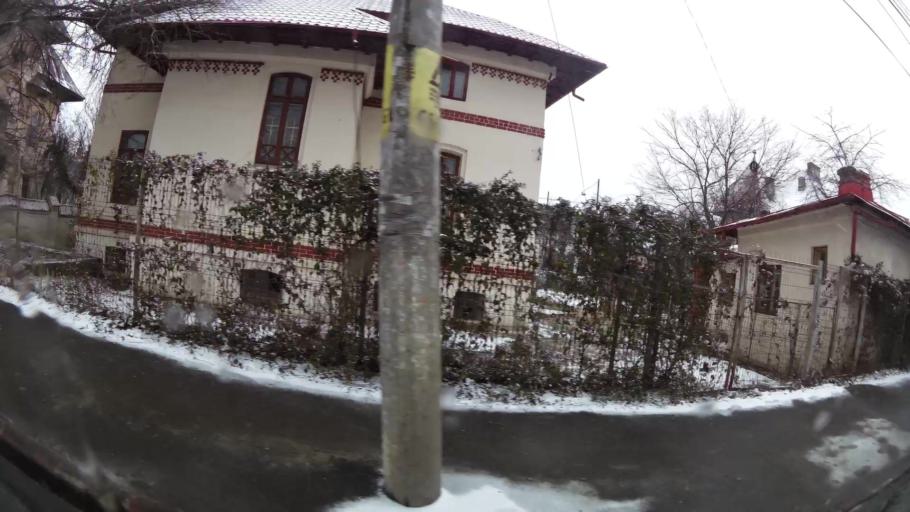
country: RO
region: Dambovita
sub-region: Municipiul Targoviste
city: Targoviste
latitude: 44.9225
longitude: 25.4568
